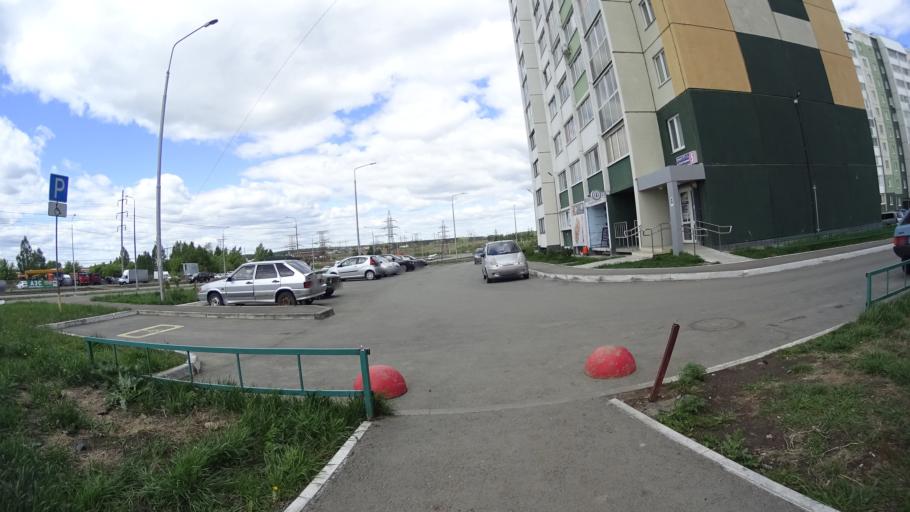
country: RU
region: Chelyabinsk
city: Roshchino
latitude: 55.1760
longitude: 61.2573
